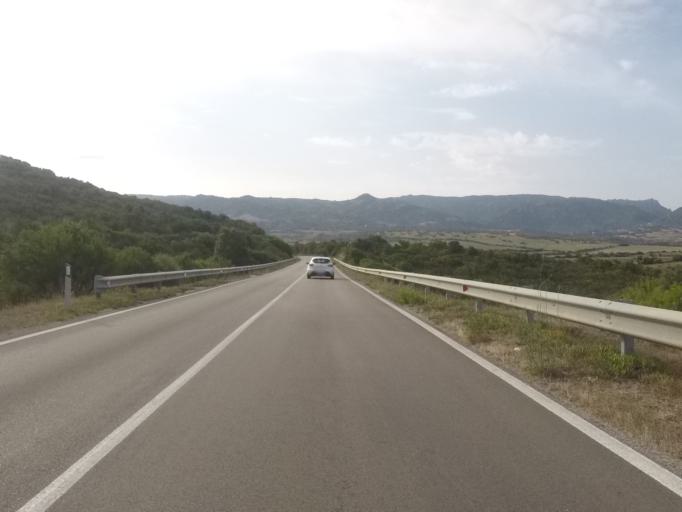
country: IT
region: Sardinia
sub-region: Provincia di Olbia-Tempio
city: Aglientu
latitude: 41.1085
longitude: 9.0619
